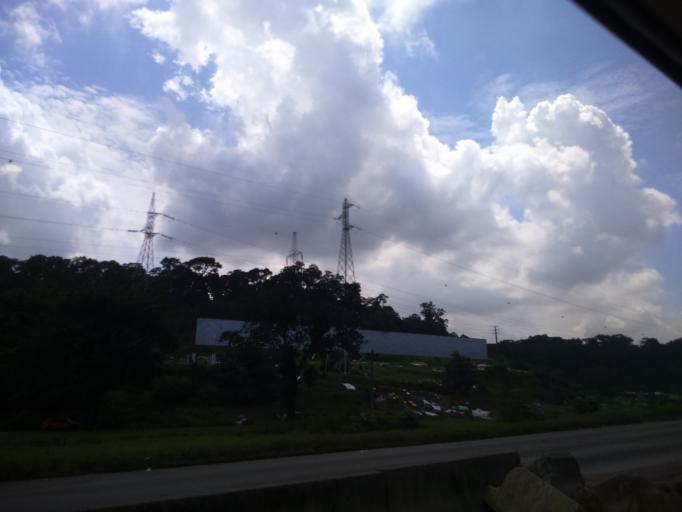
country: CI
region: Lagunes
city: Abidjan
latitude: 5.3601
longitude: -4.0408
